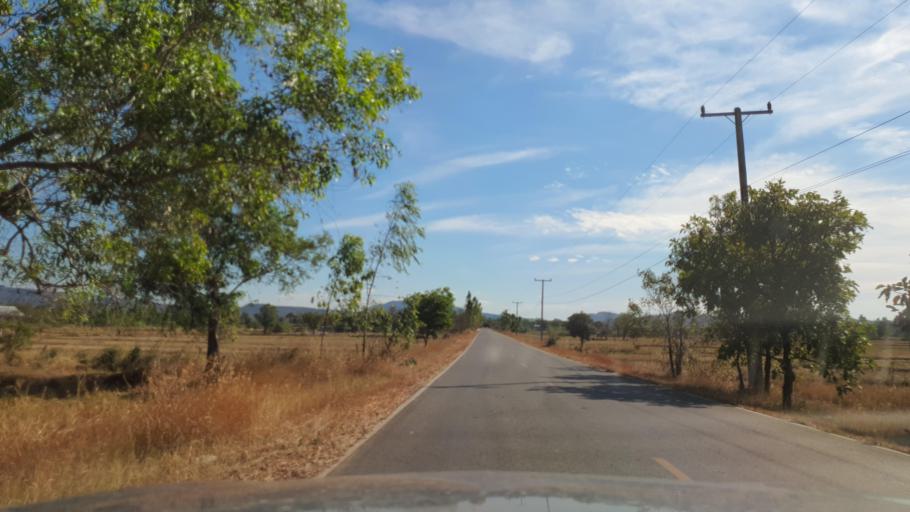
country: TH
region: Kalasin
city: Khao Wong
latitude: 16.6304
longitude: 104.1348
